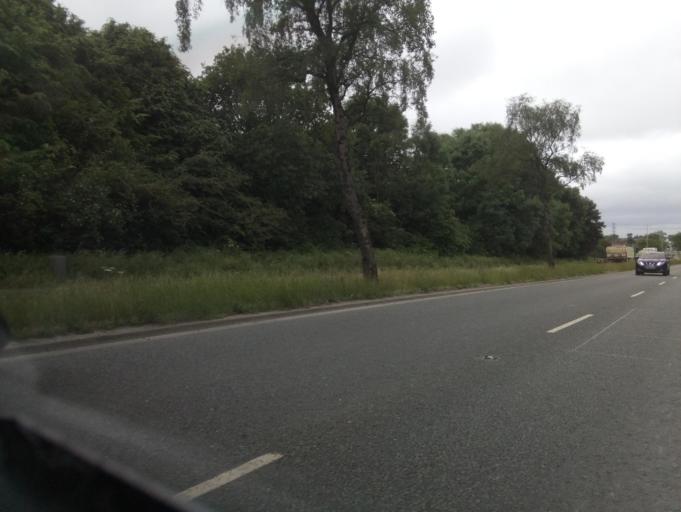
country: GB
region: England
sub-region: Leicestershire
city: Markfield
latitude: 52.7014
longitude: -1.3110
